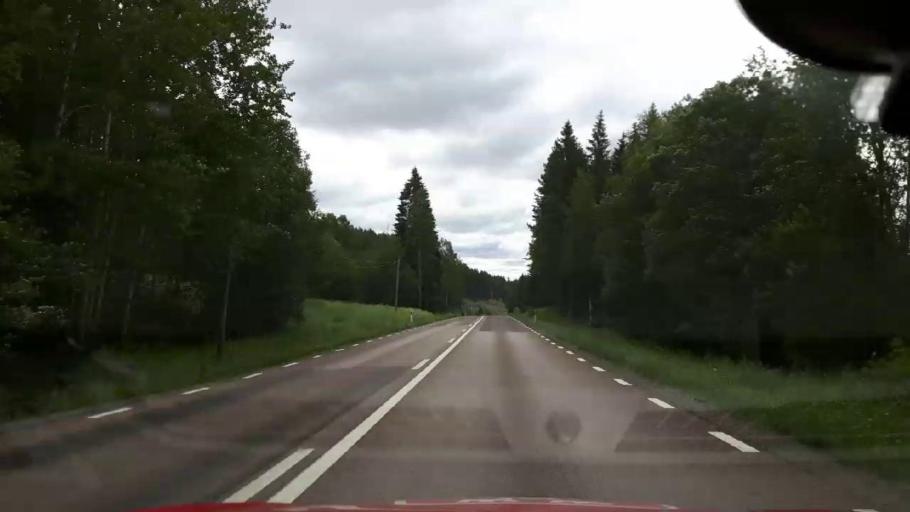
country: SE
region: Jaemtland
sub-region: OEstersunds Kommun
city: Brunflo
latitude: 62.9766
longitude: 15.0095
